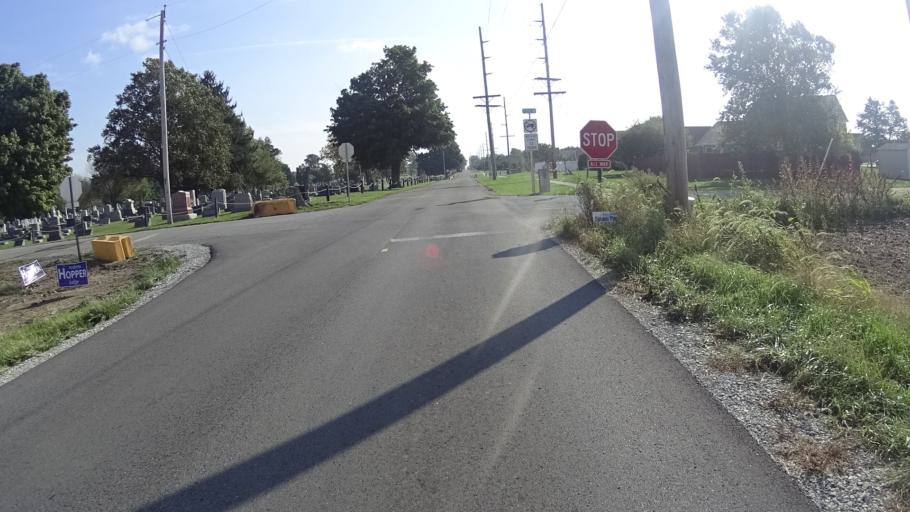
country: US
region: Indiana
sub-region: Madison County
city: Lapel
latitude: 40.0600
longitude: -85.8537
